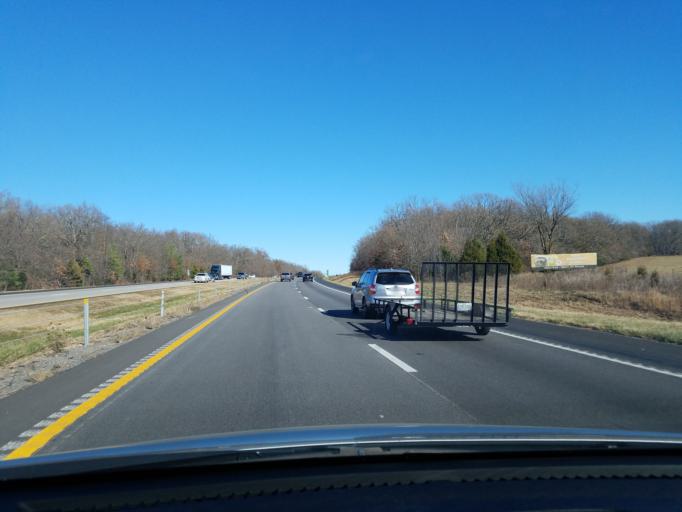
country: US
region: Missouri
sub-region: Webster County
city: Marshfield
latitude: 37.3256
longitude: -92.9569
